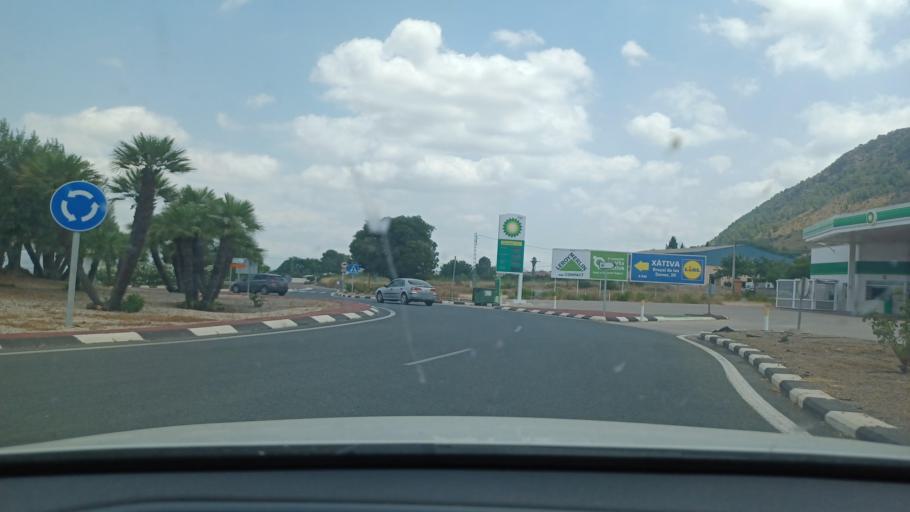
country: ES
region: Valencia
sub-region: Provincia de Valencia
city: Valles
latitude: 38.9776
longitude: -0.5533
